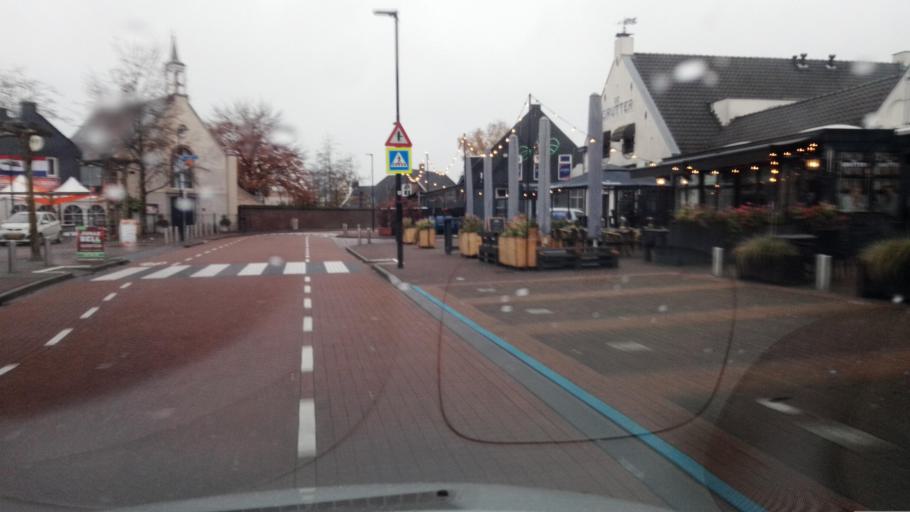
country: NL
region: North Brabant
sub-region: Gemeente Asten
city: Asten
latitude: 51.4055
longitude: 5.7471
